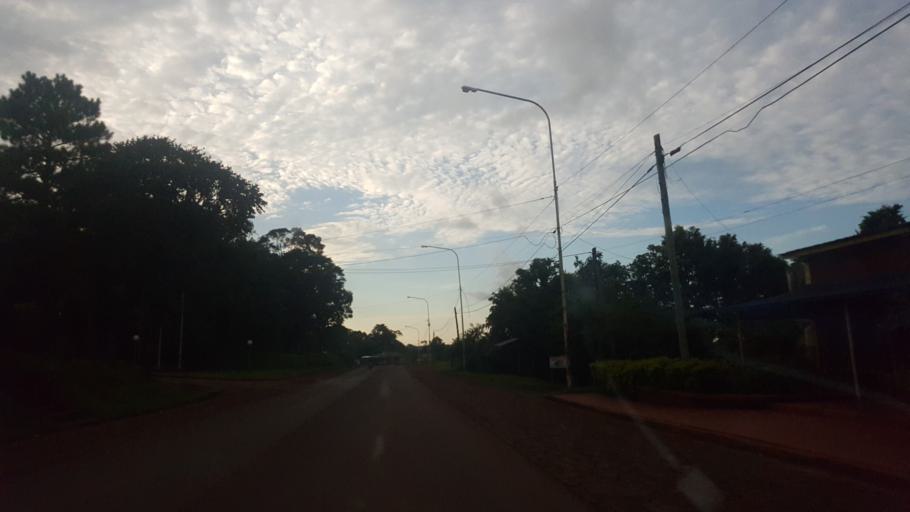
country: AR
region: Misiones
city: Dos de Mayo
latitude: -27.0291
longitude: -54.6874
